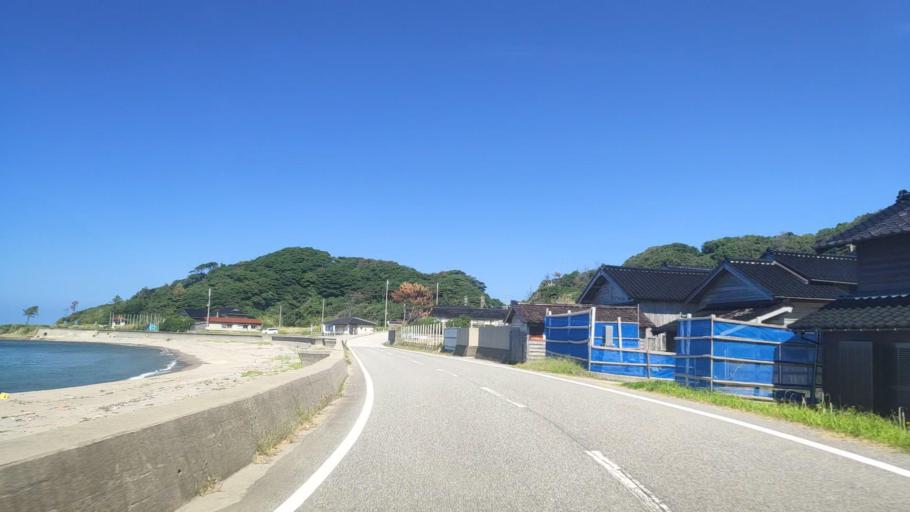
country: JP
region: Ishikawa
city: Nanao
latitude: 37.5110
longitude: 137.2193
